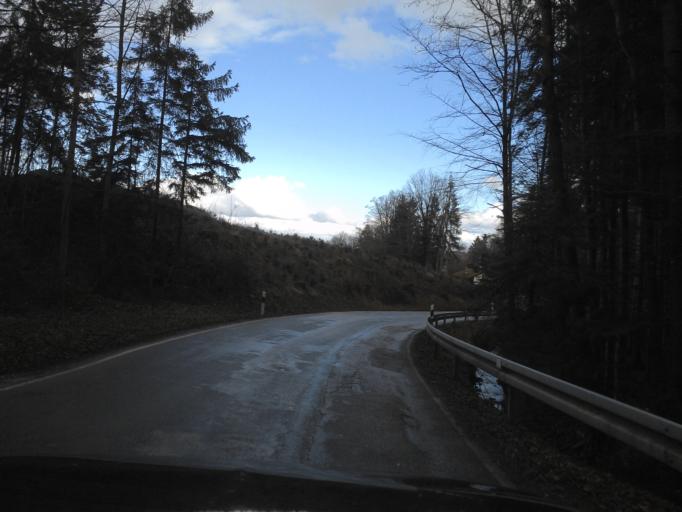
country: DE
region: Bavaria
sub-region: Upper Bavaria
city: Bad Toelz
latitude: 47.7612
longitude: 11.5316
